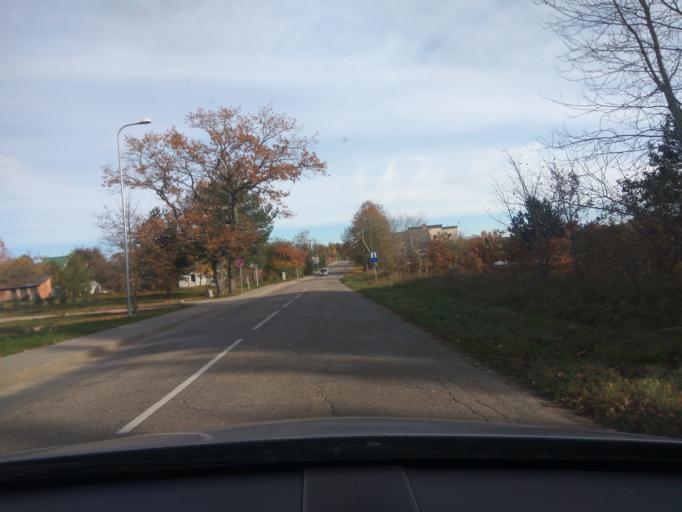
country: LV
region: Alsunga
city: Alsunga
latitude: 56.9803
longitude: 21.5579
